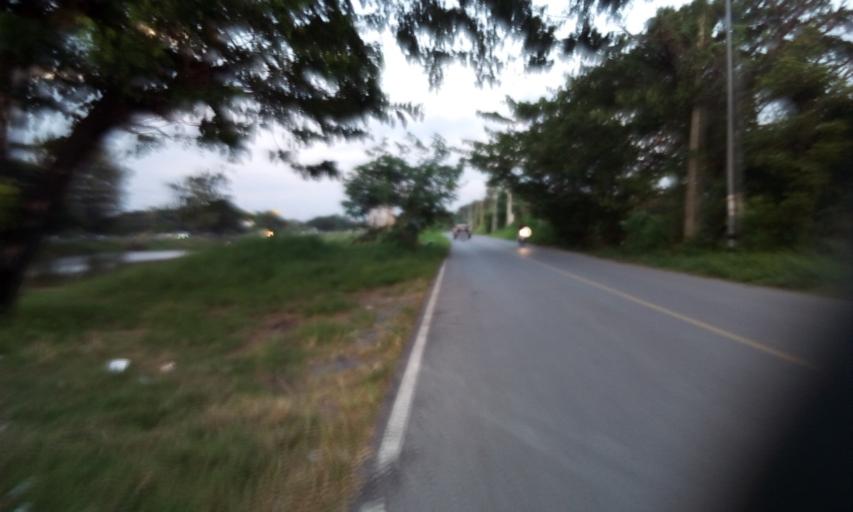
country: TH
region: Pathum Thani
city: Ban Rangsit
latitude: 14.0486
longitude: 100.8146
